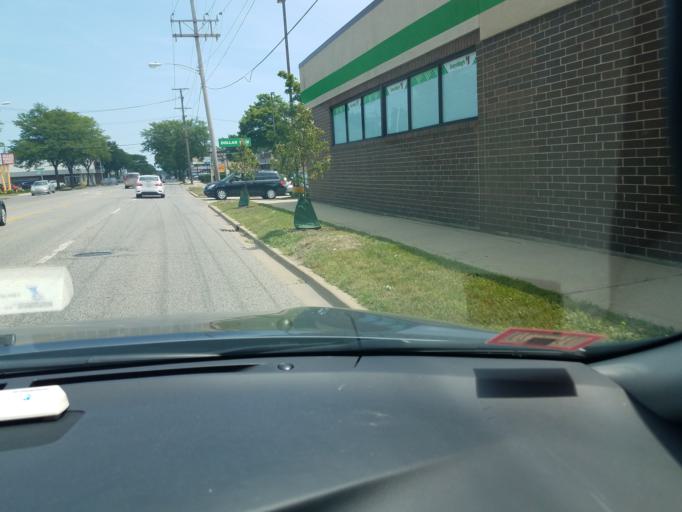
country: US
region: Illinois
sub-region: Cook County
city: Skokie
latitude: 42.0407
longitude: -87.7311
